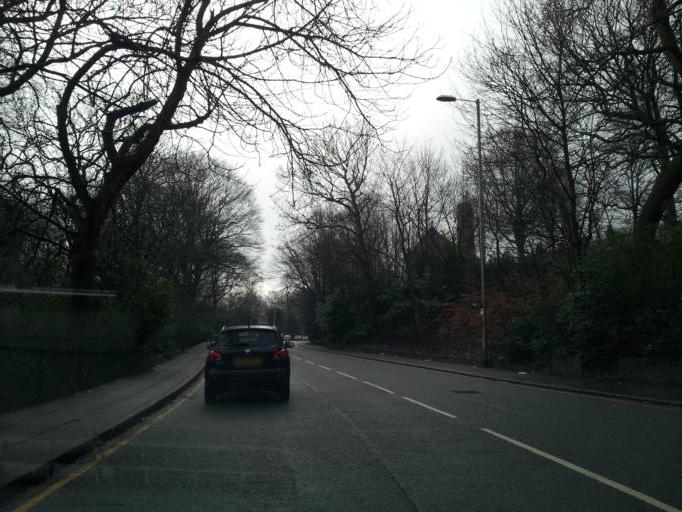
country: GB
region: England
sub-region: Manchester
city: Blackley
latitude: 53.5205
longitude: -2.2142
